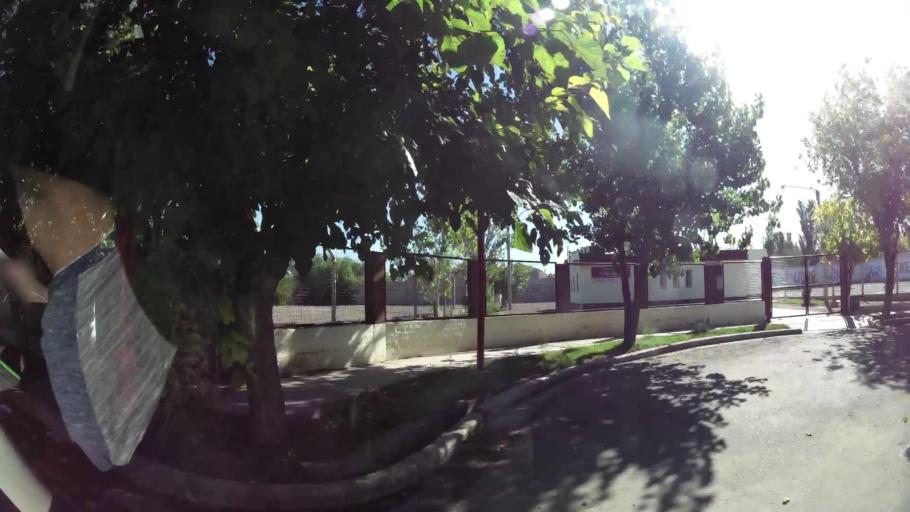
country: AR
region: San Juan
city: Villa Paula de Sarmiento
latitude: -31.5082
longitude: -68.5234
